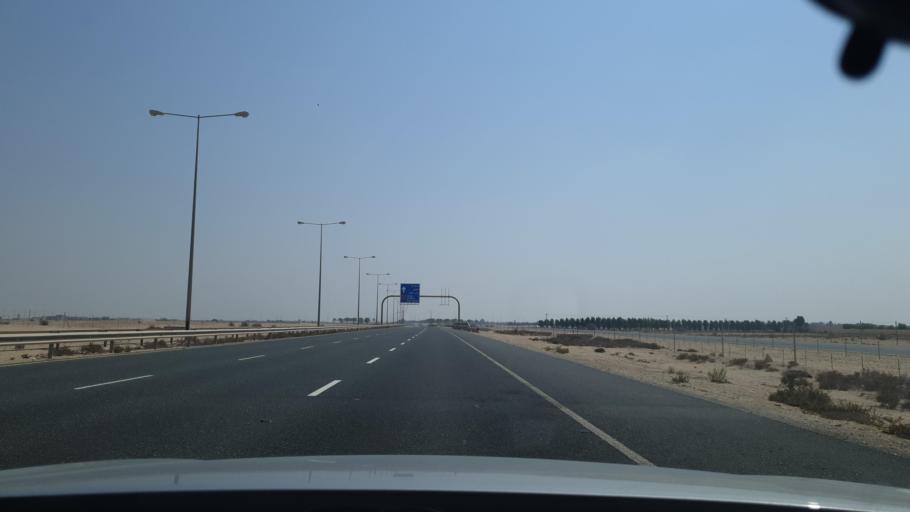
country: QA
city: Al Ghuwayriyah
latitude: 25.7933
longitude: 51.3889
